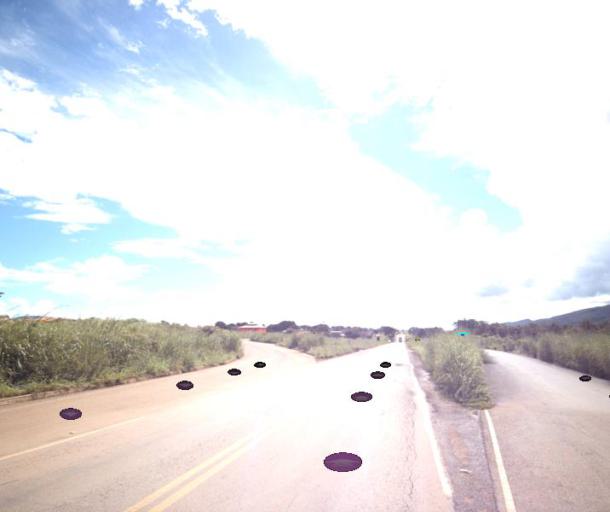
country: BR
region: Goias
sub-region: Pirenopolis
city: Pirenopolis
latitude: -16.0205
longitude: -49.1082
